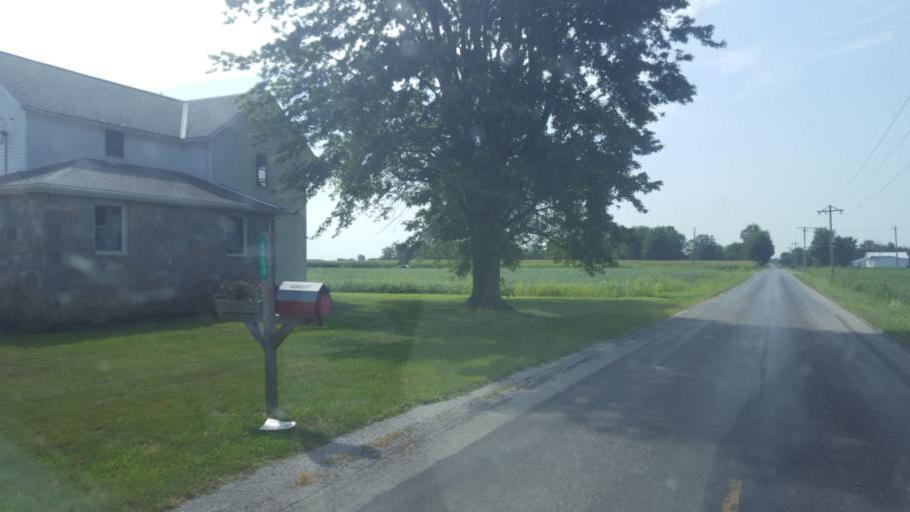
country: US
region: Ohio
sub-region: Morrow County
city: Cardington
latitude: 40.5297
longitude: -82.9957
